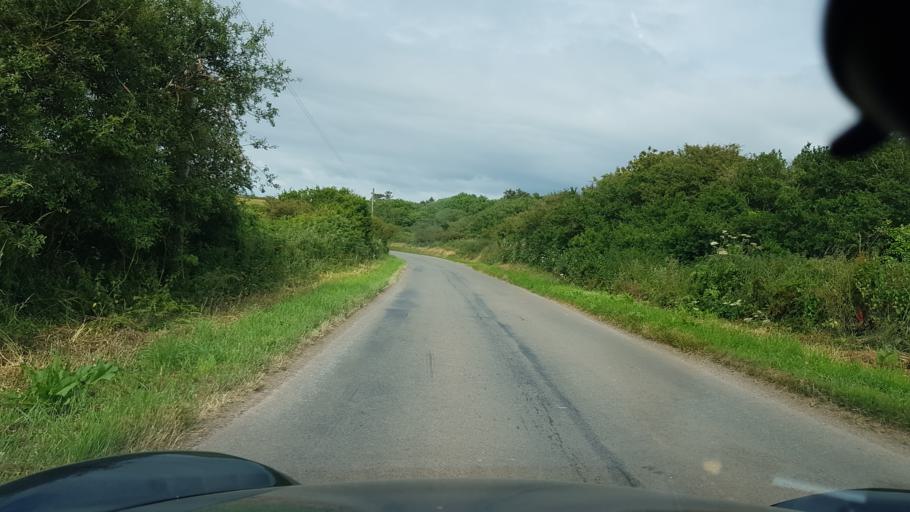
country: GB
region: Wales
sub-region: Pembrokeshire
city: Dale
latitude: 51.7356
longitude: -5.1593
